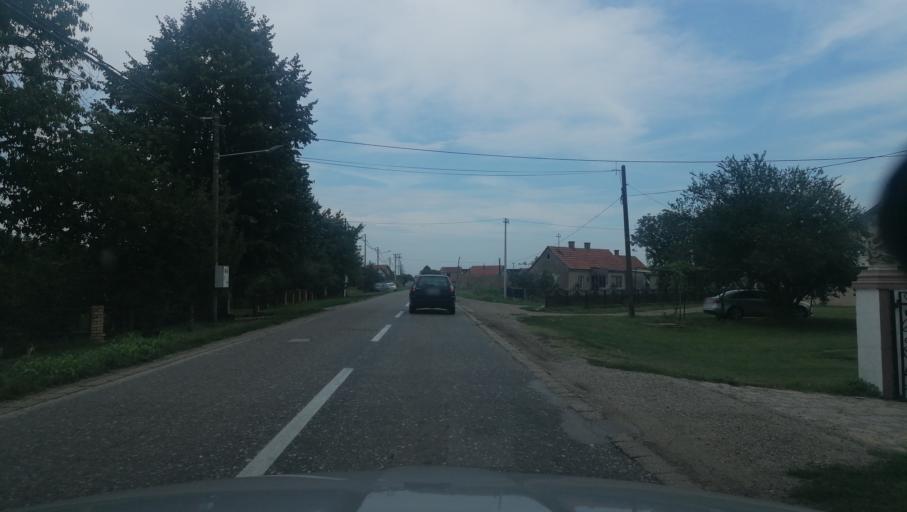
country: RS
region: Central Serbia
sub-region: Macvanski Okrug
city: Bogatic
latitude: 44.8282
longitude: 19.4629
